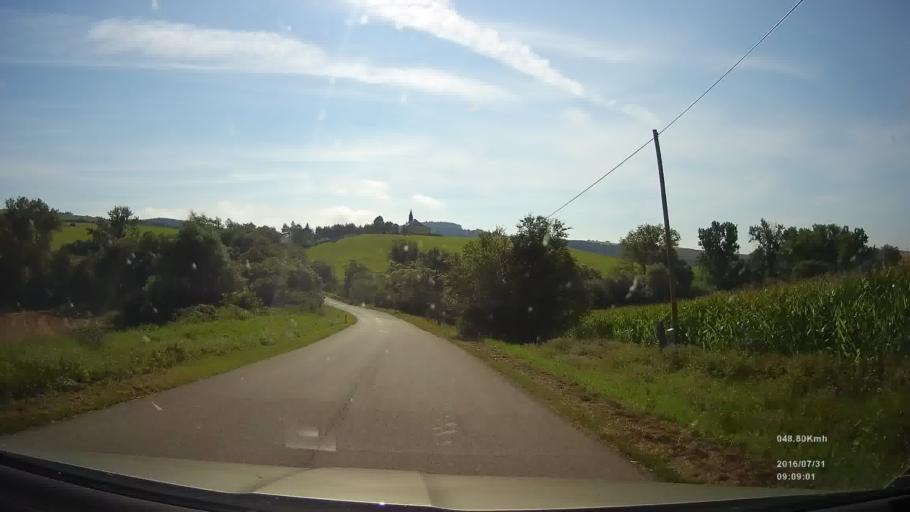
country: SK
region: Presovsky
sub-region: Okres Bardejov
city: Bardejov
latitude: 49.1860
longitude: 21.3108
